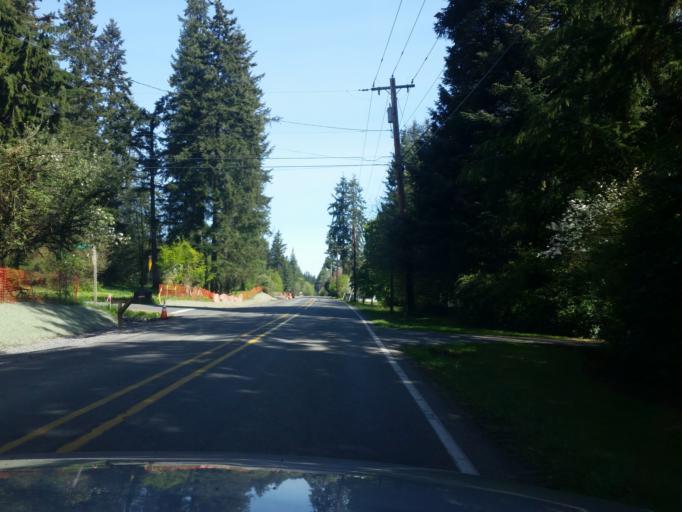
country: US
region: Washington
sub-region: Snohomish County
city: Maltby
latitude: 47.8226
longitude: -122.1097
